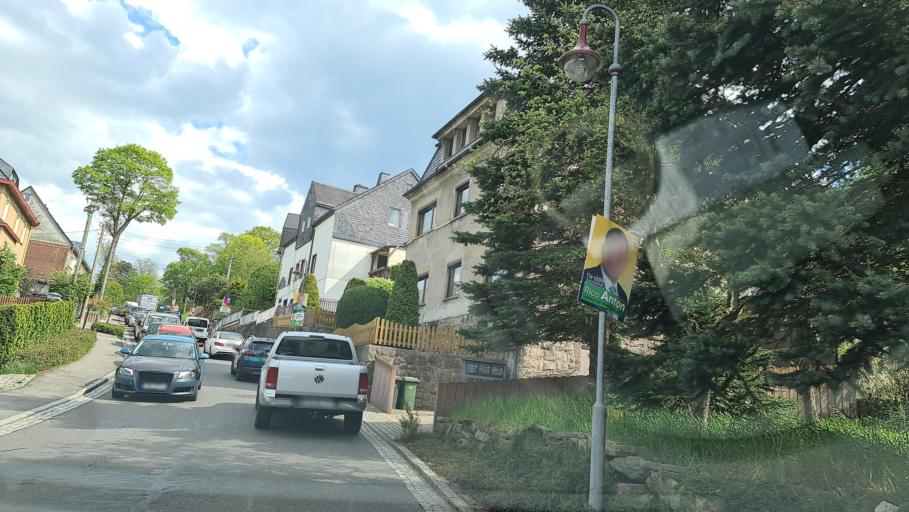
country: DE
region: Saxony
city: Lauter
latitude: 50.5600
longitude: 12.7432
